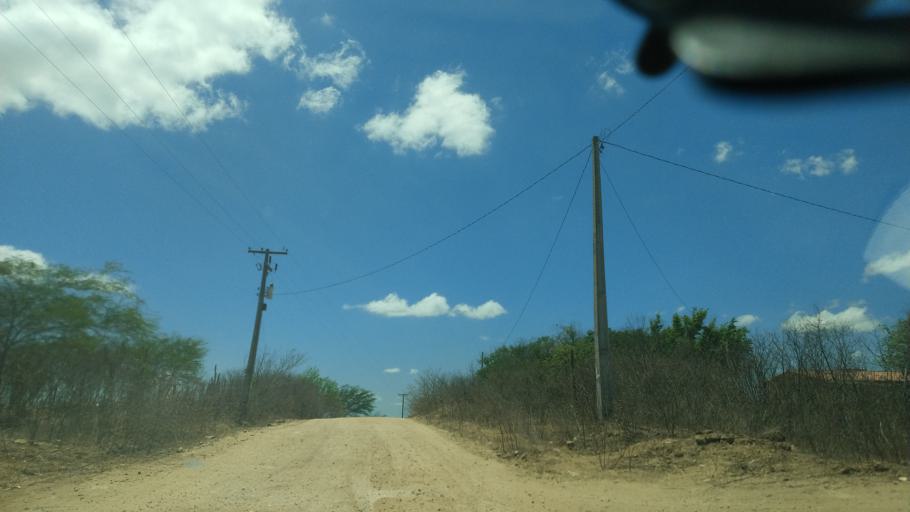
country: BR
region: Rio Grande do Norte
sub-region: Cerro Cora
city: Cerro Cora
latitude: -6.0174
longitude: -36.3296
